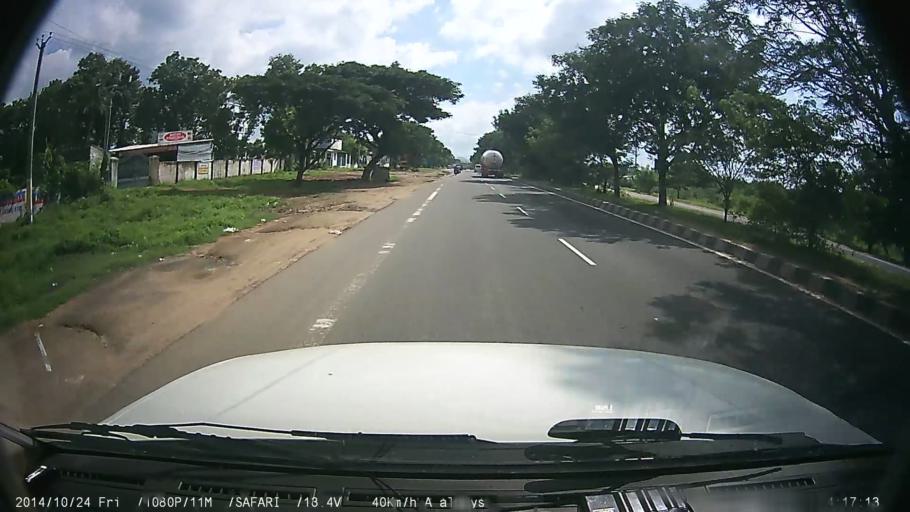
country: IN
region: Tamil Nadu
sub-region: Kancheepuram
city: Singapperumalkovil
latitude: 12.7742
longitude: 80.0093
